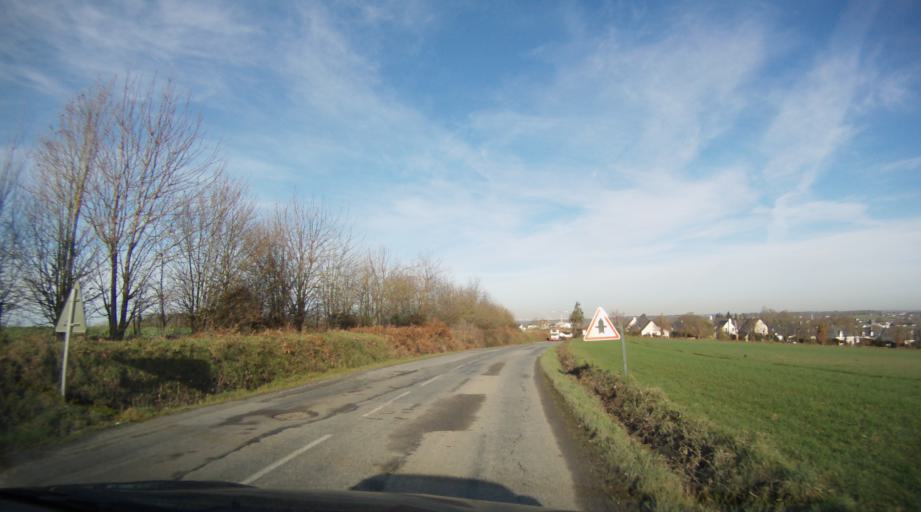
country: FR
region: Brittany
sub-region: Departement d'Ille-et-Vilaine
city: Bourgbarre
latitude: 47.9860
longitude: -1.6177
